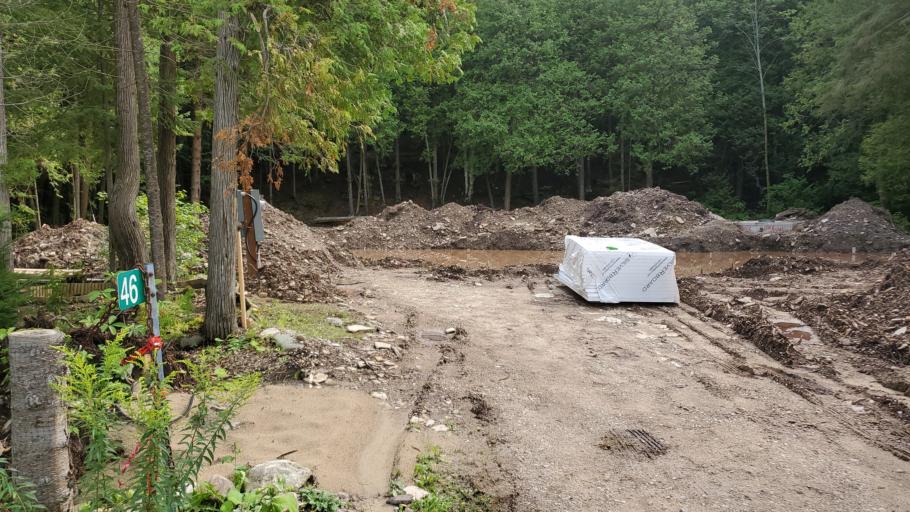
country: CA
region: Ontario
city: Owen Sound
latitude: 44.9013
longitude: -81.1517
